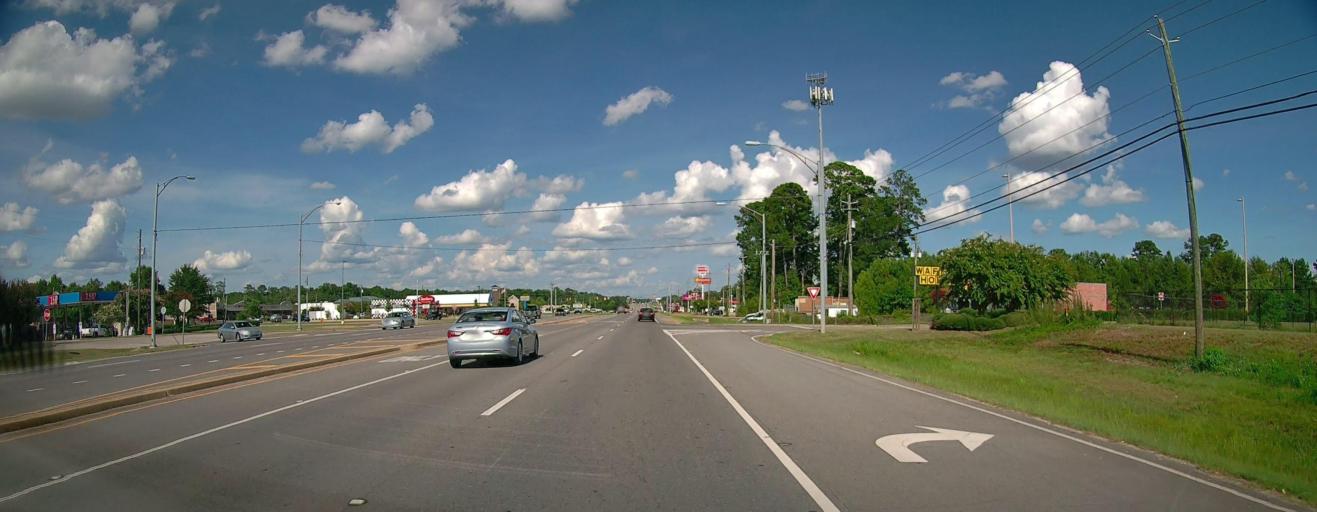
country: US
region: Alabama
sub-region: Tuscaloosa County
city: Northport
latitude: 33.2348
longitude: -87.6142
